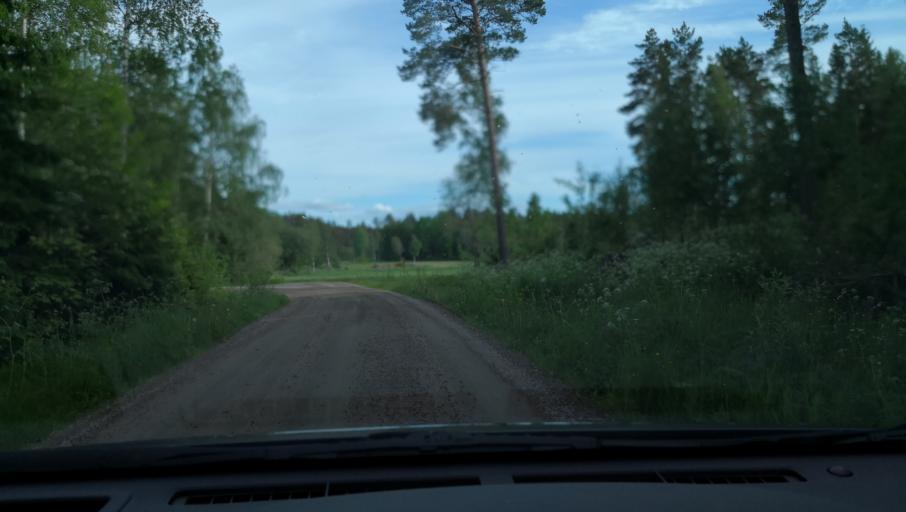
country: SE
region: Vaestmanland
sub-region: Kungsors Kommun
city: Kungsoer
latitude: 59.3570
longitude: 16.0602
